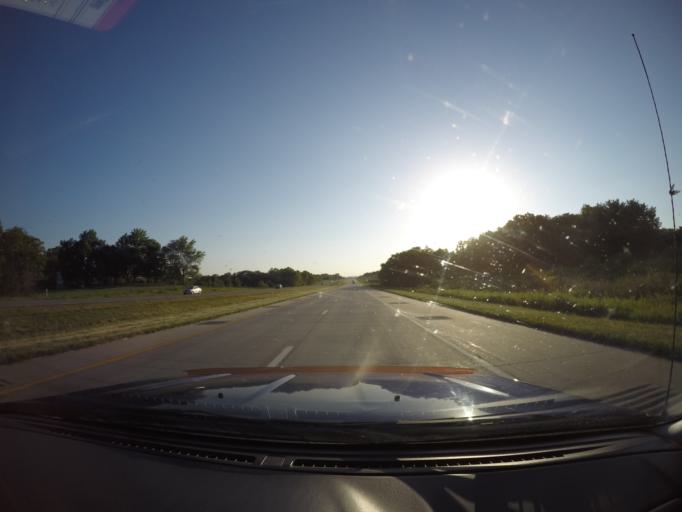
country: US
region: Kansas
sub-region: Riley County
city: Manhattan
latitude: 39.1985
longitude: -96.4609
